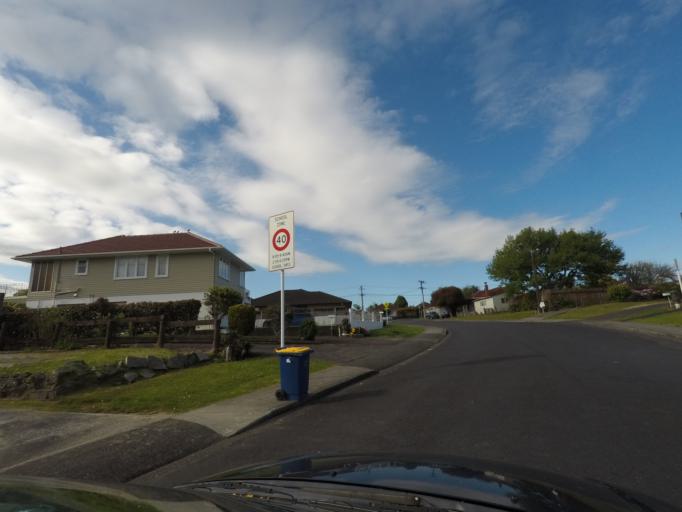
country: NZ
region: Auckland
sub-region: Auckland
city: Rosebank
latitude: -36.8704
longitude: 174.6447
